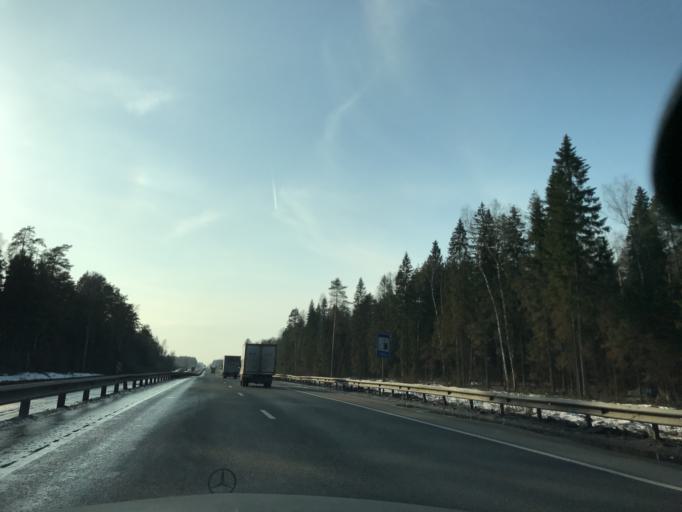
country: RU
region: Vladimir
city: Stepantsevo
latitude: 56.2309
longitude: 41.7473
